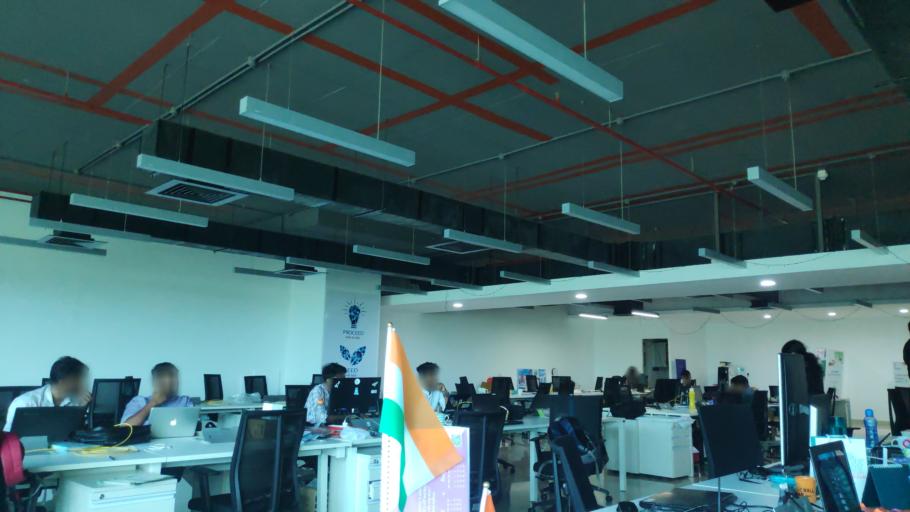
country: IN
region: Kerala
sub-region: Kozhikode
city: Kozhikode
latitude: 11.2552
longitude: 75.8284
